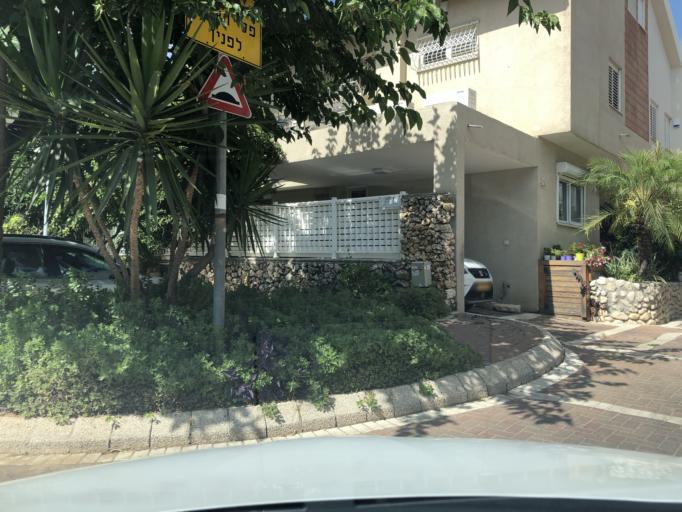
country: IL
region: Tel Aviv
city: Giv`at Shemu'el
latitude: 32.0641
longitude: 34.8470
